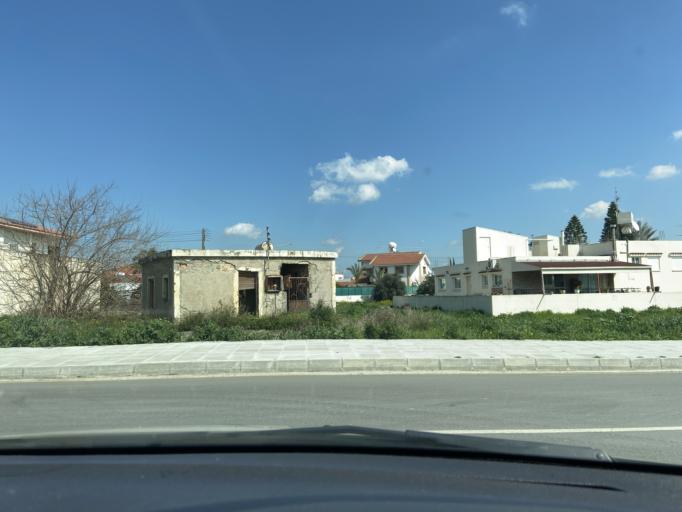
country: CY
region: Lefkosia
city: Alampra
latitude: 35.0216
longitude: 33.3870
